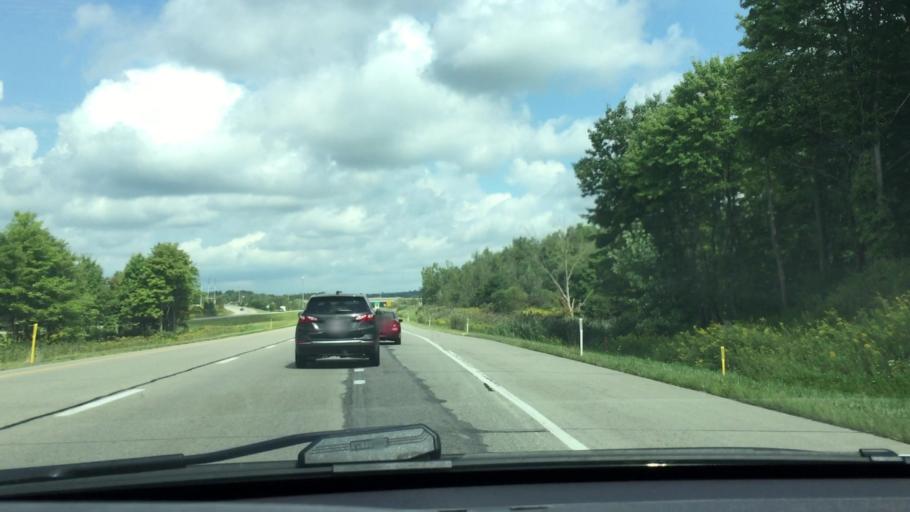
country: US
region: Pennsylvania
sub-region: Mercer County
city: Grove City
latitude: 41.1372
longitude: -80.1537
